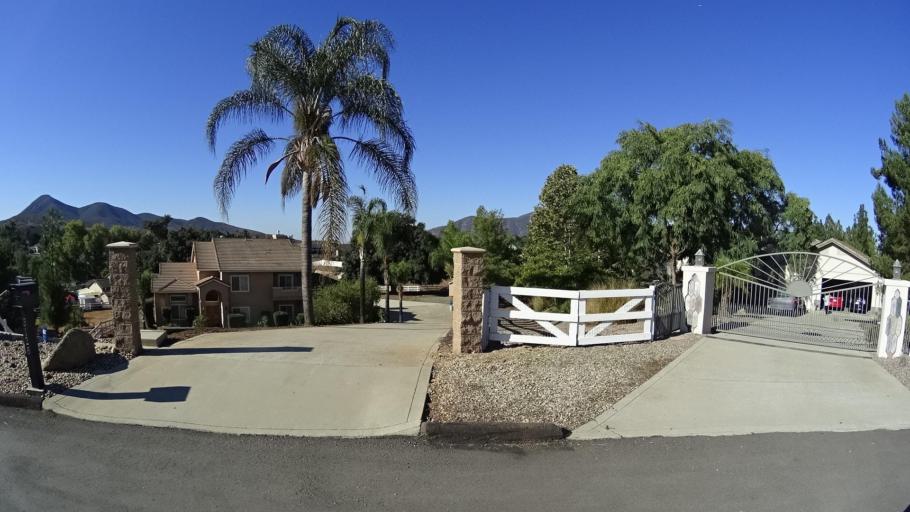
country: US
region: California
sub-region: San Diego County
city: Jamul
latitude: 32.7095
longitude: -116.8787
